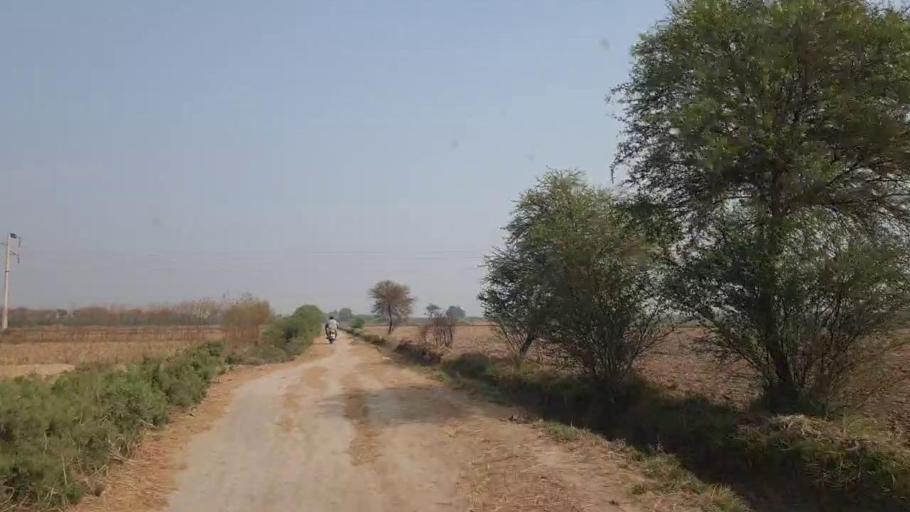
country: PK
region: Sindh
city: Matli
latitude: 25.0610
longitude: 68.6384
